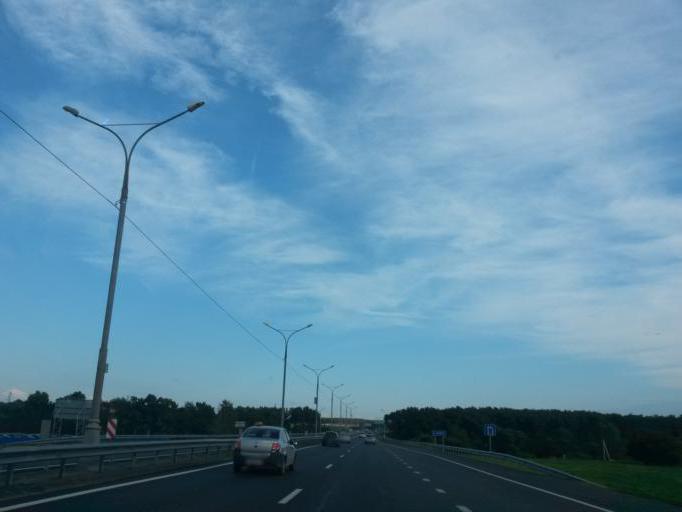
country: RU
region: Moskovskaya
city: Gorki-Leninskiye
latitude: 55.4960
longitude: 37.8432
